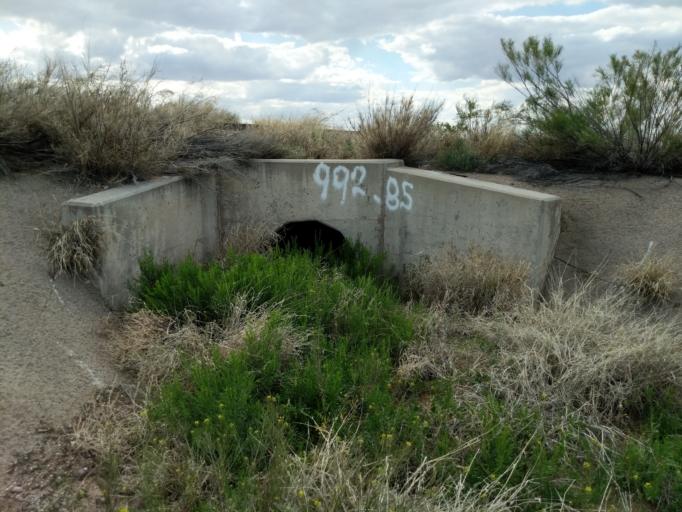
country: US
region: Arizona
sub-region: Pima County
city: Tucson
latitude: 32.1419
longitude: -110.8788
